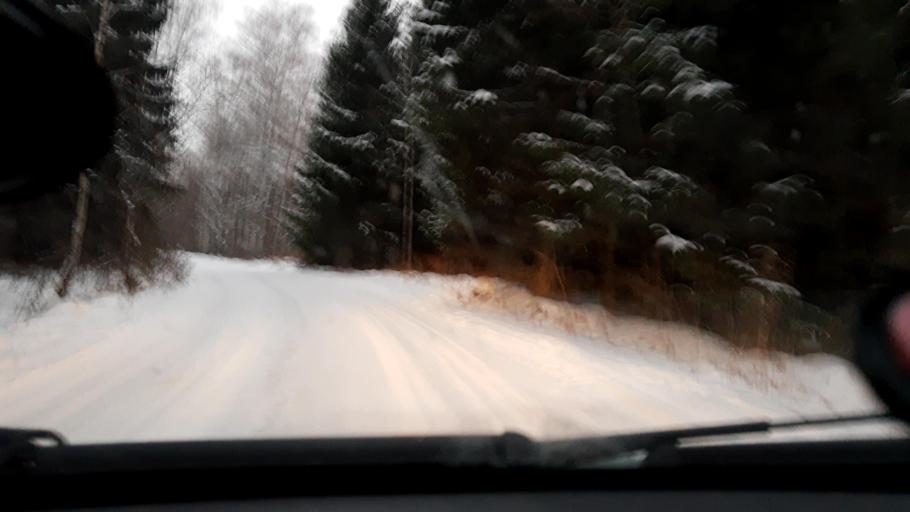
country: RU
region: Bashkortostan
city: Iglino
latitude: 54.8360
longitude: 56.2201
